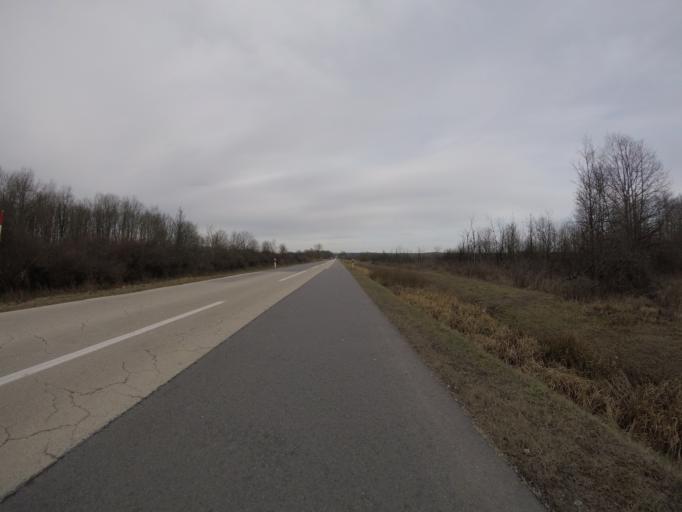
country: HR
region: Grad Zagreb
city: Horvati
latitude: 45.5568
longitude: 15.8597
